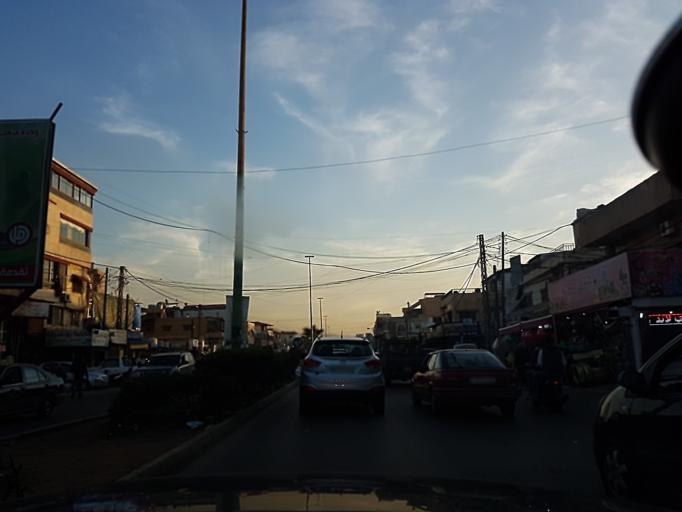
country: LB
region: Beyrouth
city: Beirut
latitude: 33.8465
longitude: 35.4850
